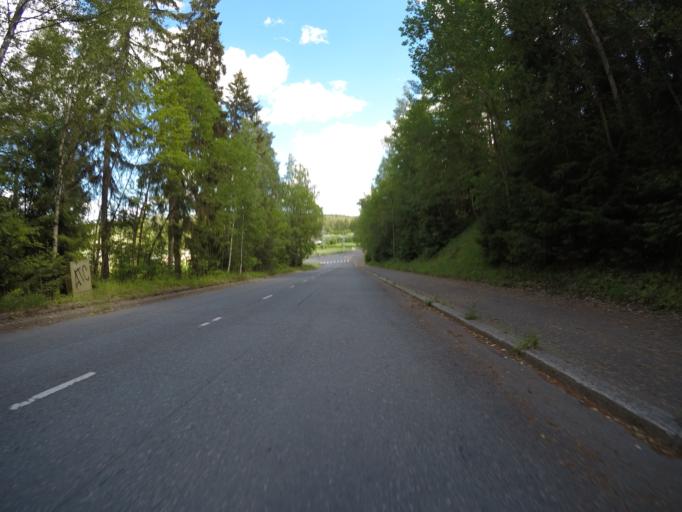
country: FI
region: Haeme
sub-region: Haemeenlinna
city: Haemeenlinna
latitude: 61.0173
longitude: 24.4337
